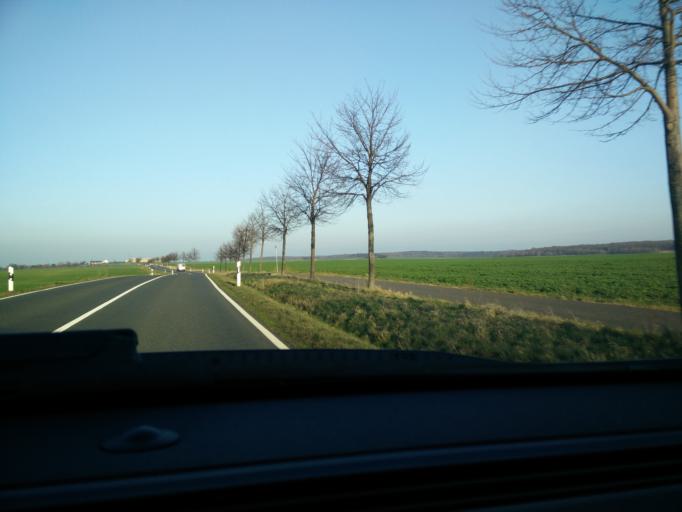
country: DE
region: Saxony
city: Grossbardau
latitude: 51.1867
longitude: 12.6925
